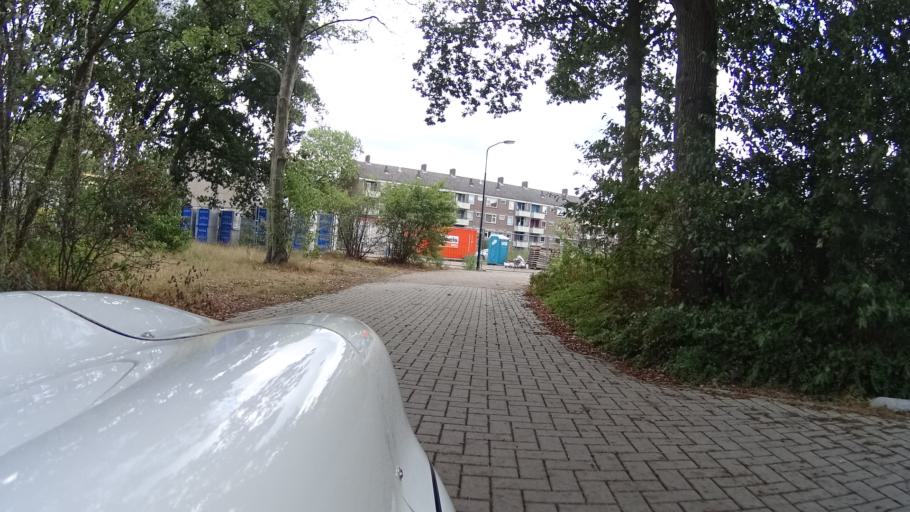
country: NL
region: Utrecht
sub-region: Gemeente De Bilt
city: De Bilt
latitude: 52.1230
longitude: 5.1797
